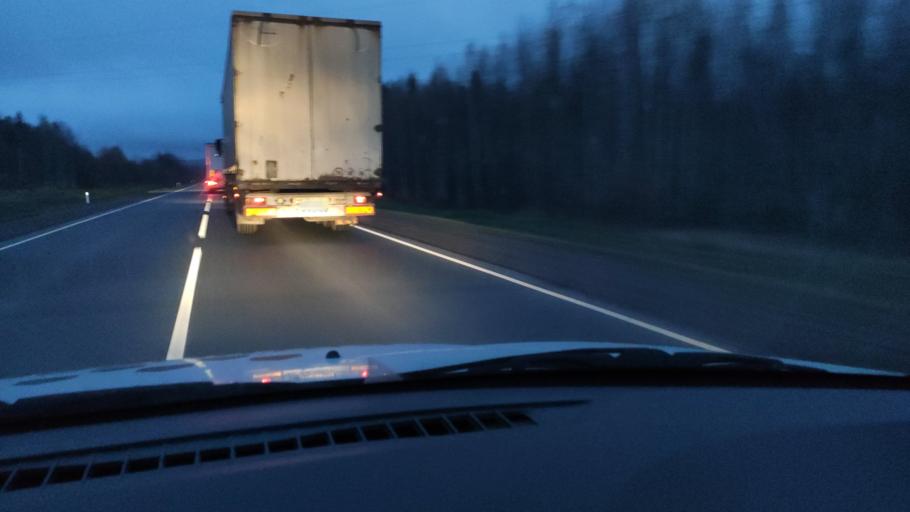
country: RU
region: Kirov
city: Kostino
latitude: 58.8324
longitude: 53.5103
